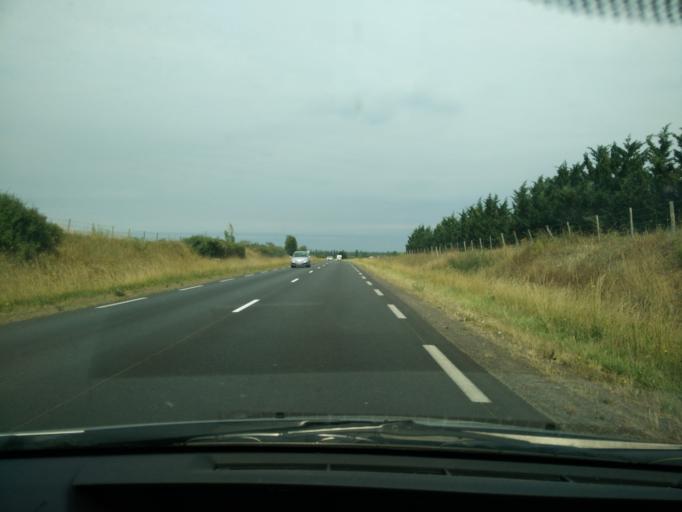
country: FR
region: Pays de la Loire
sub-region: Departement de Maine-et-Loire
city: Doue-la-Fontaine
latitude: 47.1829
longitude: -0.2887
